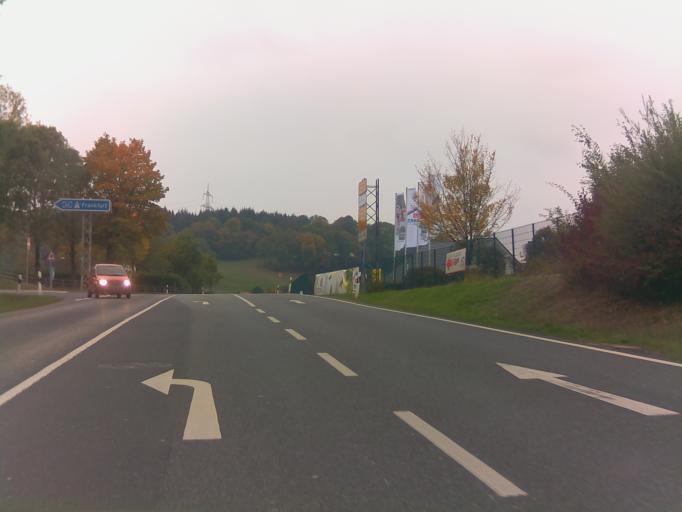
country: DE
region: Hesse
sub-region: Regierungsbezirk Darmstadt
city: Schluchtern
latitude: 50.3844
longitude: 9.5265
